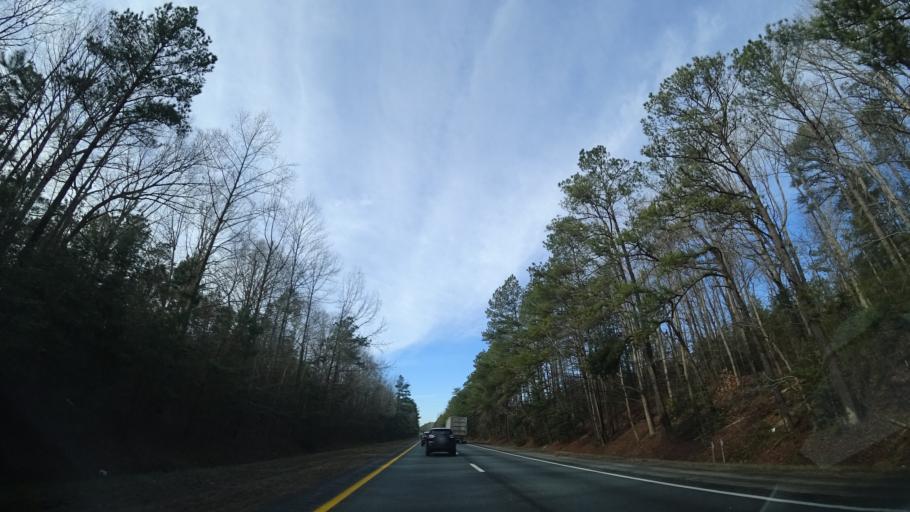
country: US
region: Virginia
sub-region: New Kent County
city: New Kent
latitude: 37.4850
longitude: -76.9580
